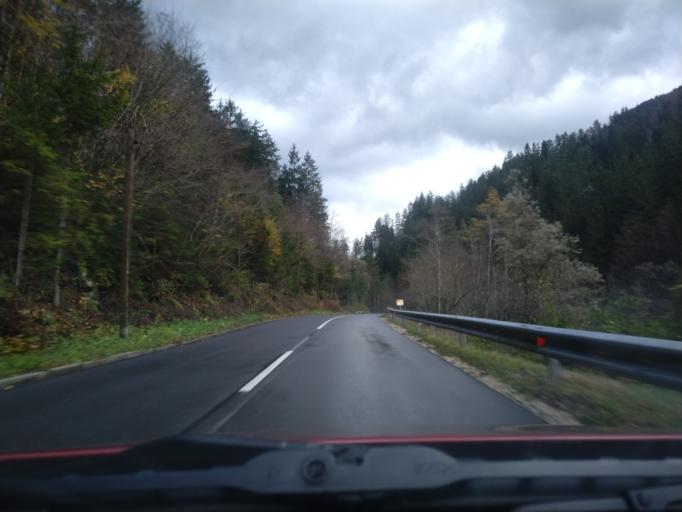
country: SI
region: Solcava
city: Solcava
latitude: 46.3887
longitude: 14.7170
